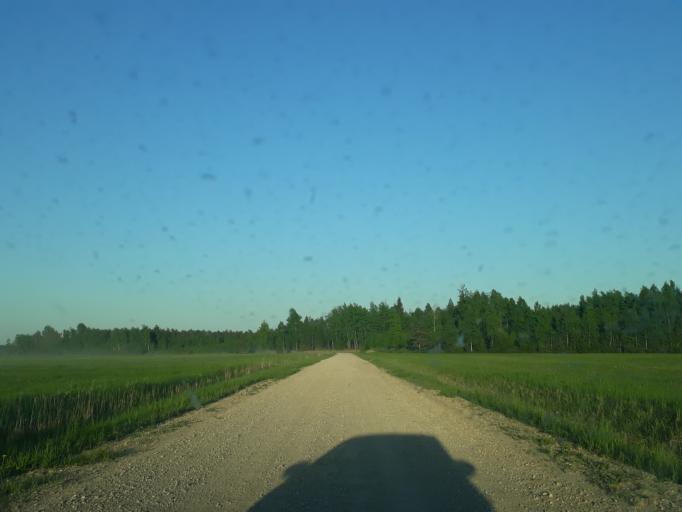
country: EE
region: Paernumaa
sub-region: Tootsi vald
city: Tootsi
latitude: 58.5804
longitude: 24.9117
